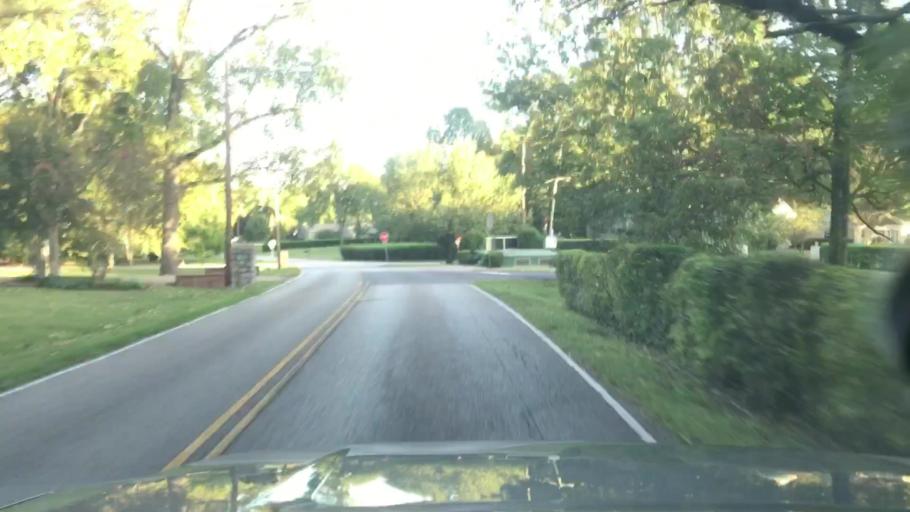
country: US
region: Tennessee
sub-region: Davidson County
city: Belle Meade
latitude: 36.1283
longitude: -86.8629
